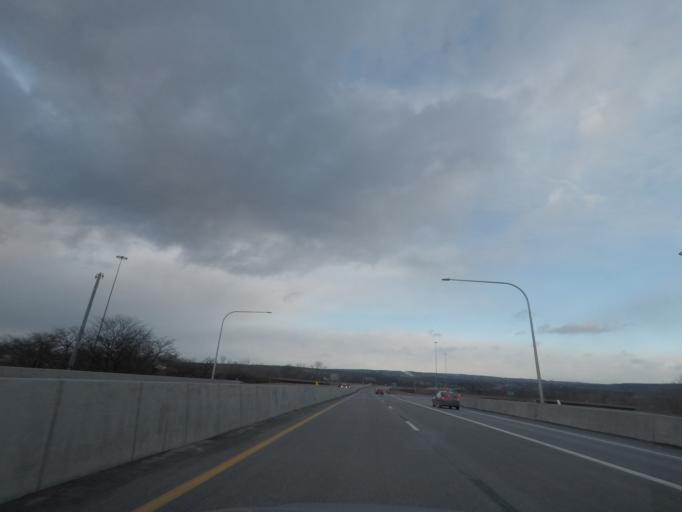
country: US
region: New York
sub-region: Oneida County
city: Utica
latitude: 43.1058
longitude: -75.2390
